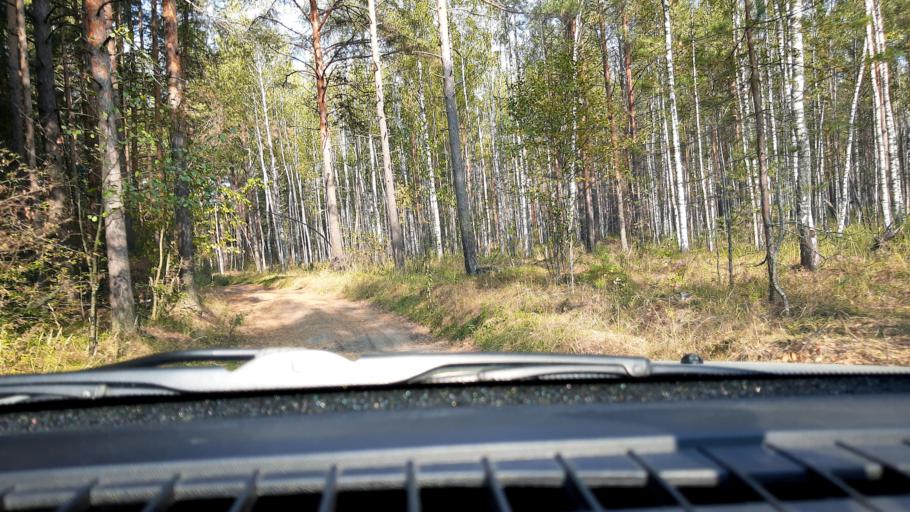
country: RU
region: Nizjnij Novgorod
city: Lukino
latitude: 56.3895
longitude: 43.6287
